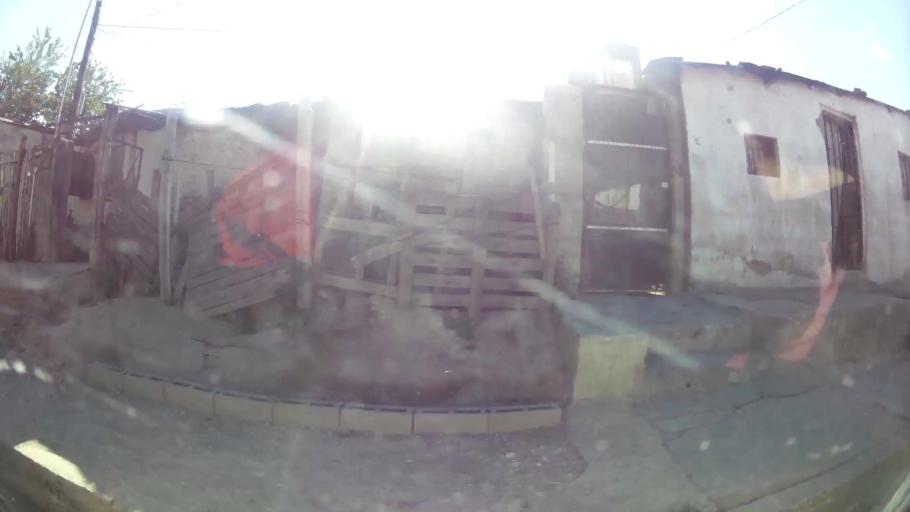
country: AR
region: Cordoba
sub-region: Departamento de Capital
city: Cordoba
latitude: -31.3753
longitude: -64.1893
